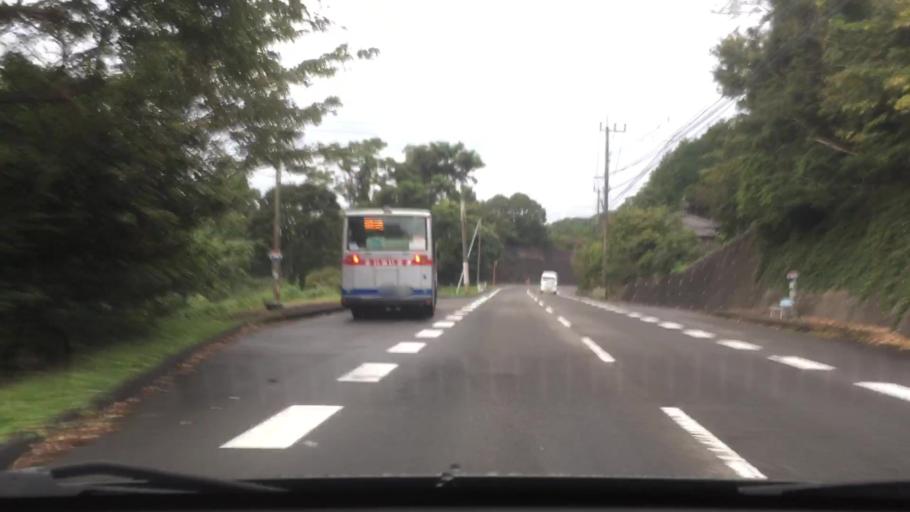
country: JP
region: Nagasaki
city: Sasebo
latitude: 32.9800
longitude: 129.7145
